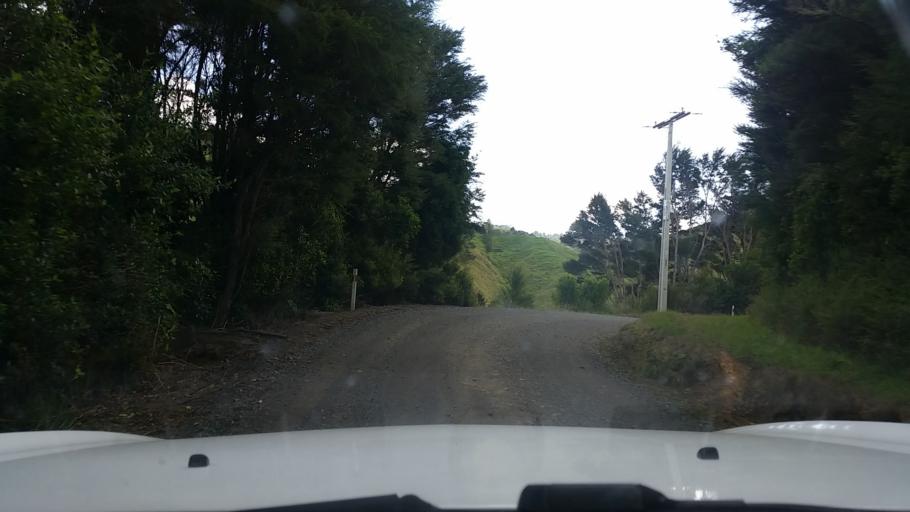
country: NZ
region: Waikato
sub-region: Hauraki District
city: Ngatea
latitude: -37.4826
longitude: 175.4520
